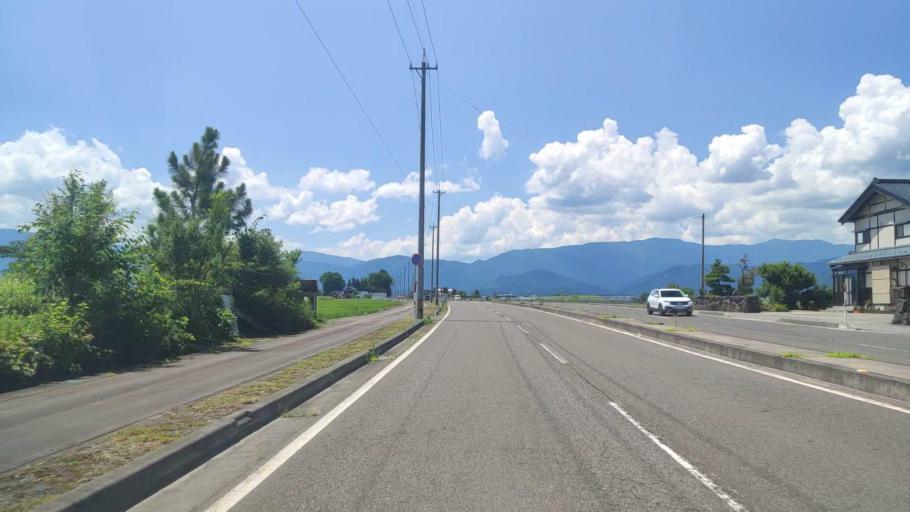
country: JP
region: Fukui
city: Ono
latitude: 36.0014
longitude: 136.5089
